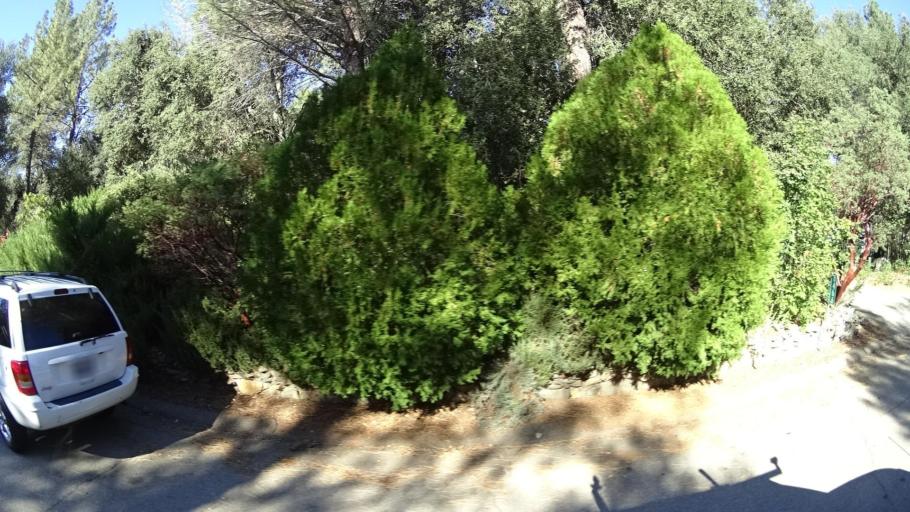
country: US
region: California
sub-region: San Diego County
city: Pine Valley
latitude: 32.8393
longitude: -116.5251
